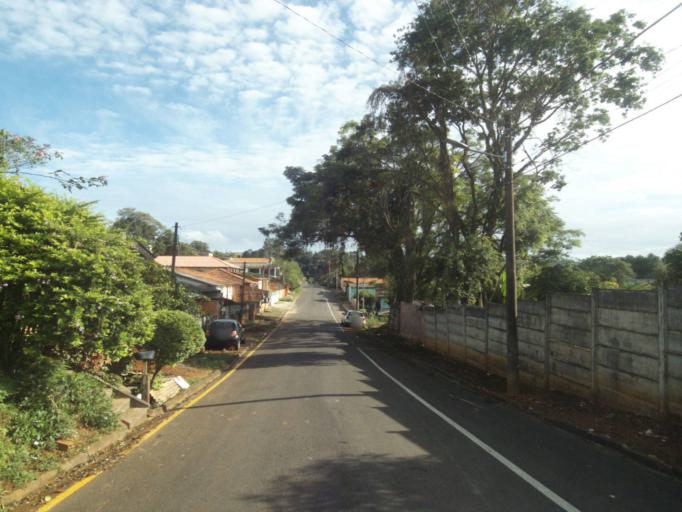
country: BR
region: Parana
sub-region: Telemaco Borba
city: Telemaco Borba
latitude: -24.3473
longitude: -50.6111
